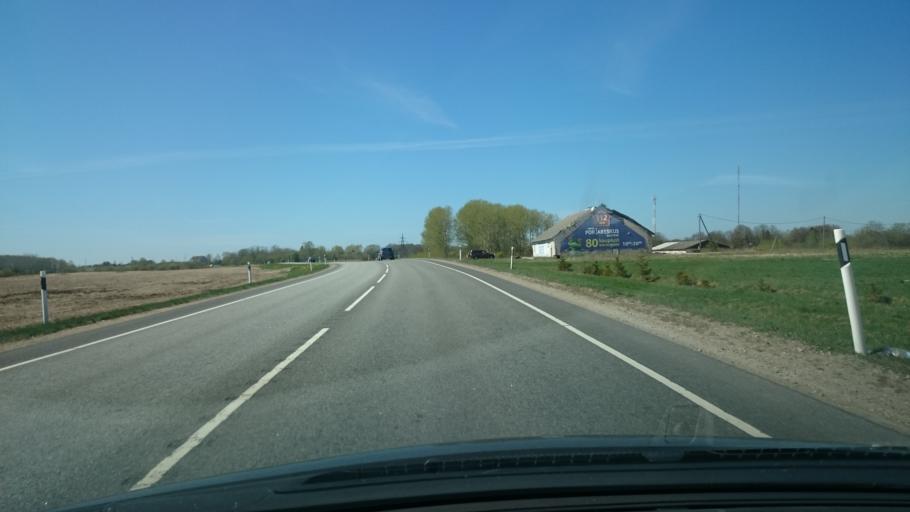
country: EE
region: Ida-Virumaa
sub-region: Narva-Joesuu linn
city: Narva-Joesuu
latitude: 59.3985
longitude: 28.0746
